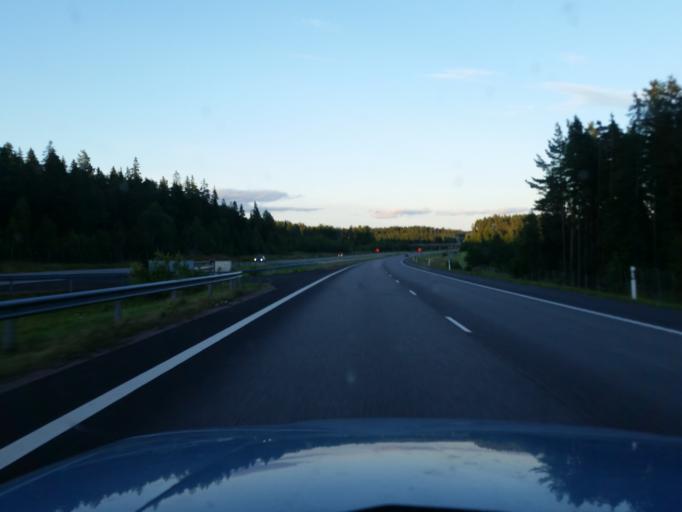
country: FI
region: Varsinais-Suomi
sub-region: Turku
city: Paimio
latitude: 60.4281
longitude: 22.8347
